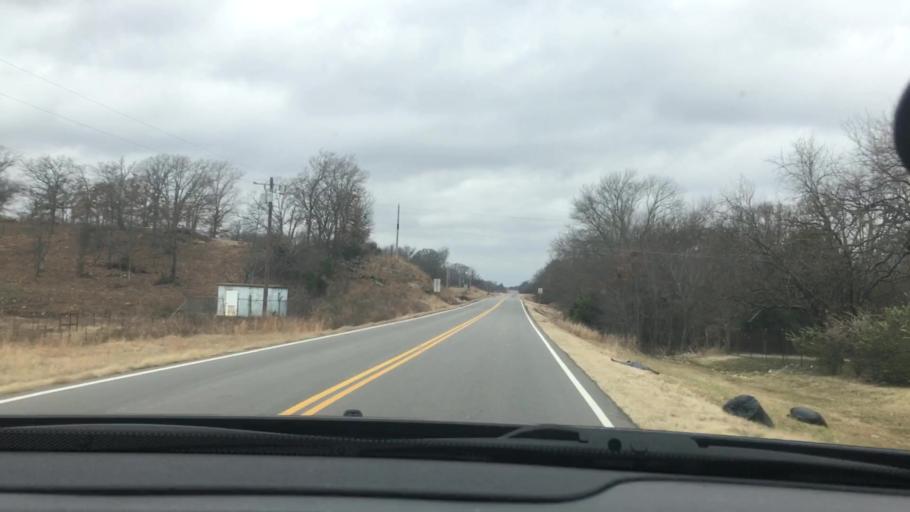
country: US
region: Oklahoma
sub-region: Atoka County
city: Atoka
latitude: 34.3749
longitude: -96.1498
